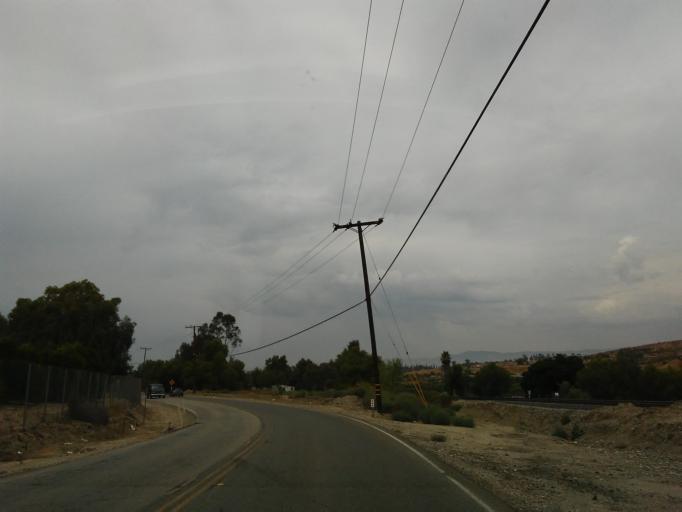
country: US
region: California
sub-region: San Bernardino County
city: Redlands
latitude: 34.0067
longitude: -117.1711
